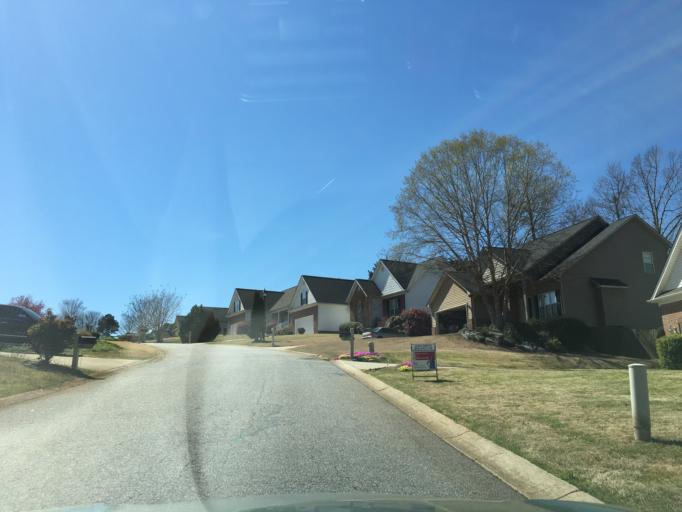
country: US
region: South Carolina
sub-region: Spartanburg County
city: Roebuck
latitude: 34.8810
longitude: -82.0411
